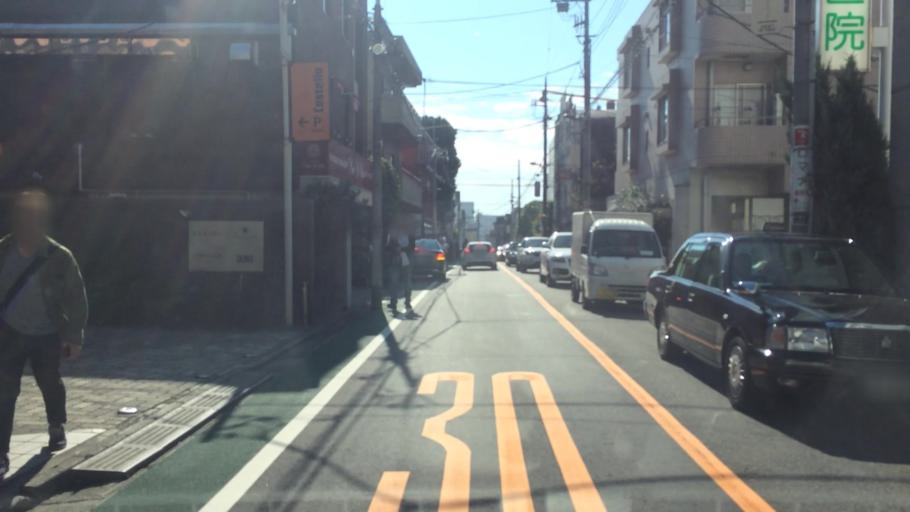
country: JP
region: Tokyo
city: Tokyo
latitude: 35.6130
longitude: 139.6666
